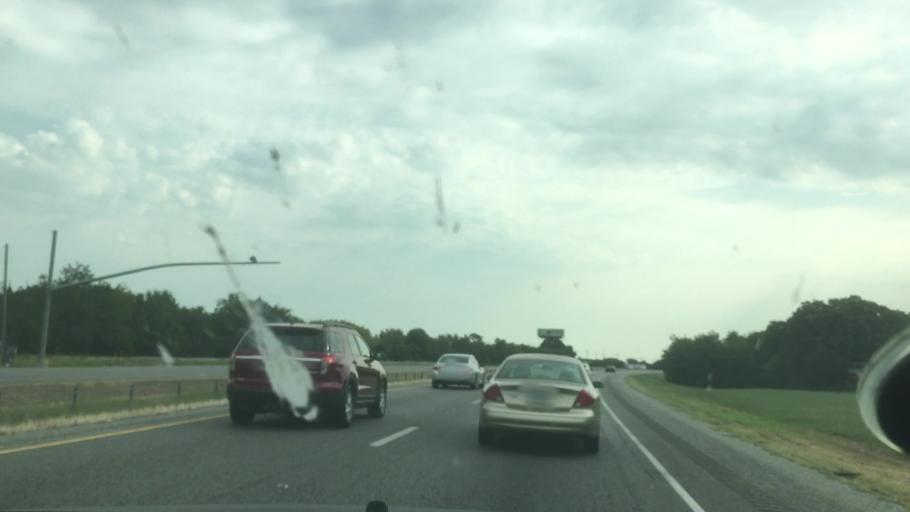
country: US
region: Oklahoma
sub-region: Bryan County
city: Colbert
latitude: 33.8713
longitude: -96.5083
